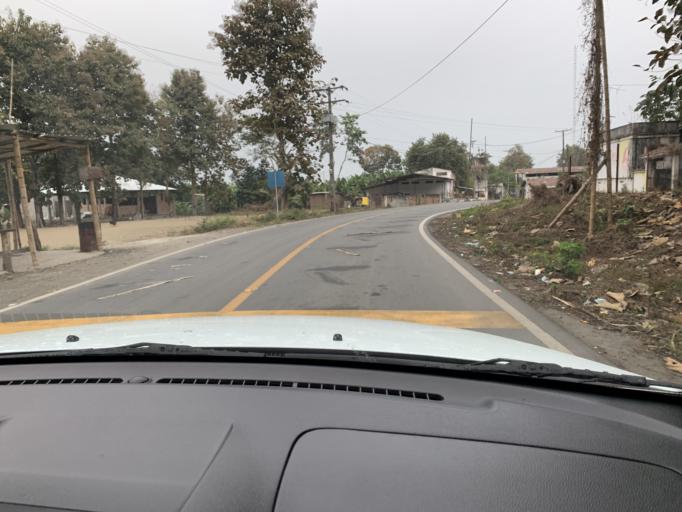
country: EC
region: Guayas
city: Coronel Marcelino Mariduena
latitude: -2.2937
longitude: -79.5020
